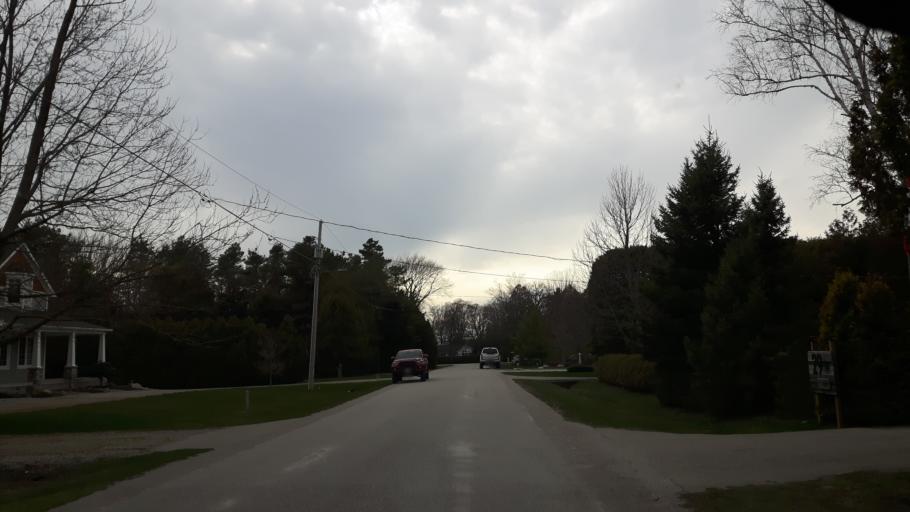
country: CA
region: Ontario
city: Bluewater
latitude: 43.5605
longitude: -81.7026
